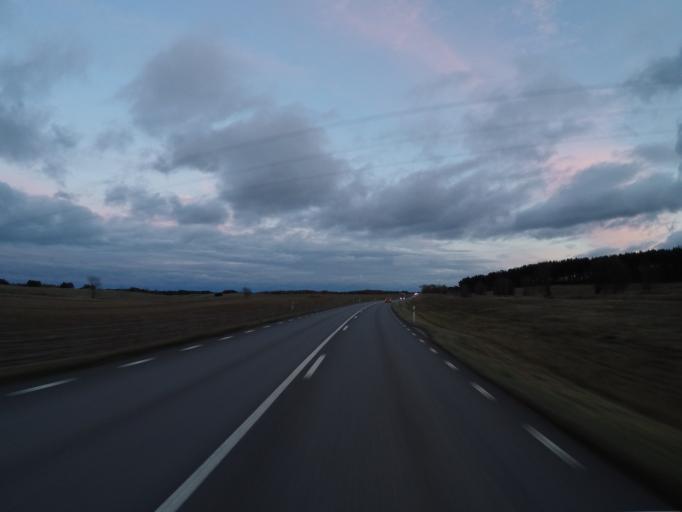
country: SE
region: Skane
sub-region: Kristianstads Kommun
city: Degeberga
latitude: 55.8234
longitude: 14.1121
